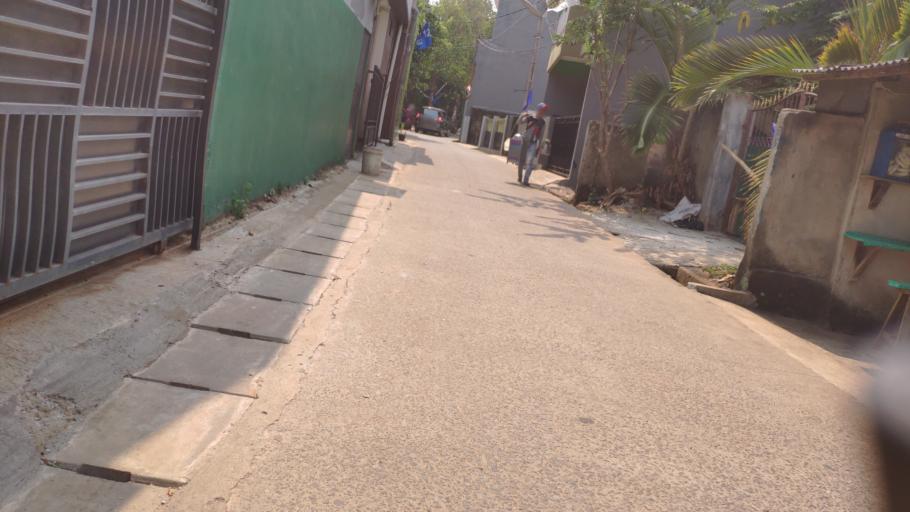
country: ID
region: West Java
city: Sawangan
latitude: -6.3822
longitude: 106.7948
